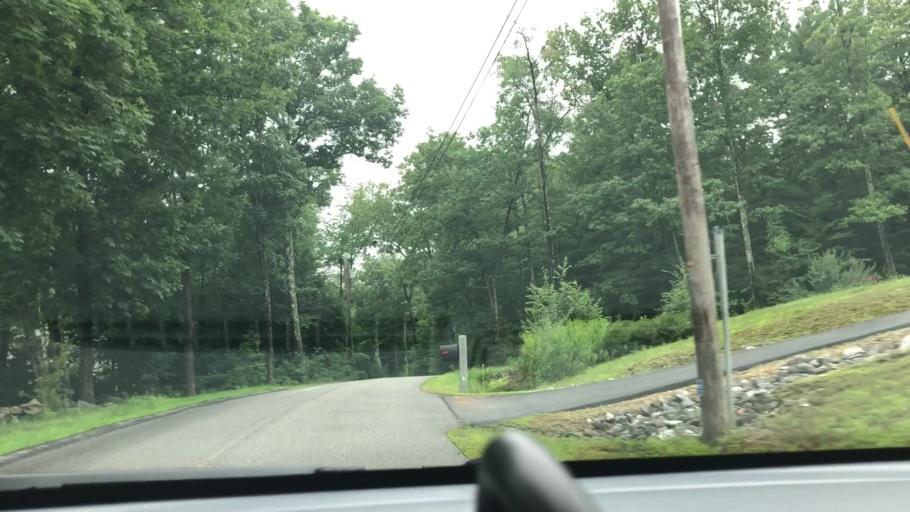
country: US
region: New Hampshire
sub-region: Hillsborough County
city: Pinardville
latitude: 42.9794
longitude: -71.5341
